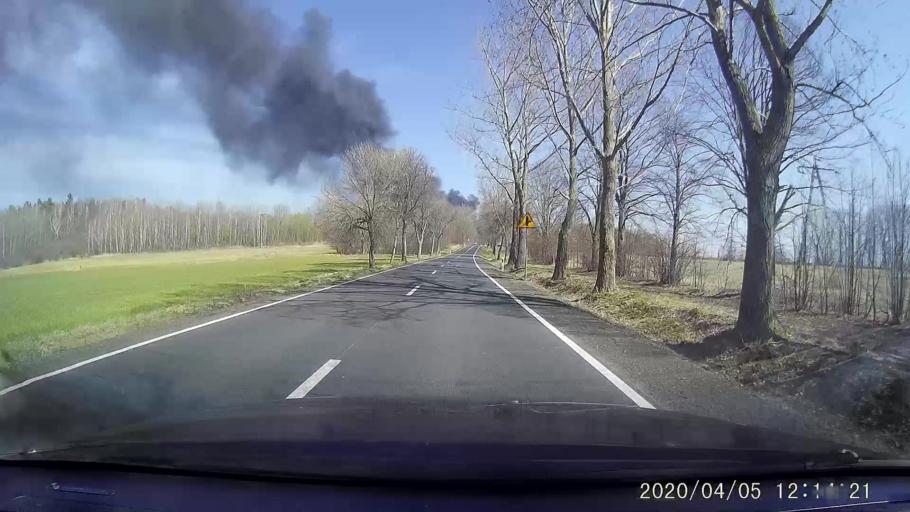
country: PL
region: Lower Silesian Voivodeship
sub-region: Powiat lwowecki
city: Gryfow Slaski
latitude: 51.0146
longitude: 15.3845
